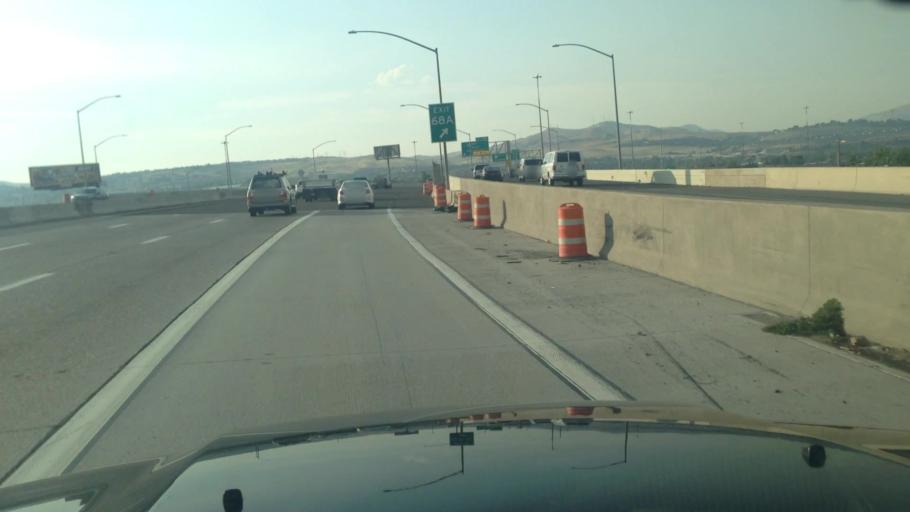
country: US
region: Nevada
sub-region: Washoe County
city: Reno
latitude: 39.5325
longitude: -119.7870
